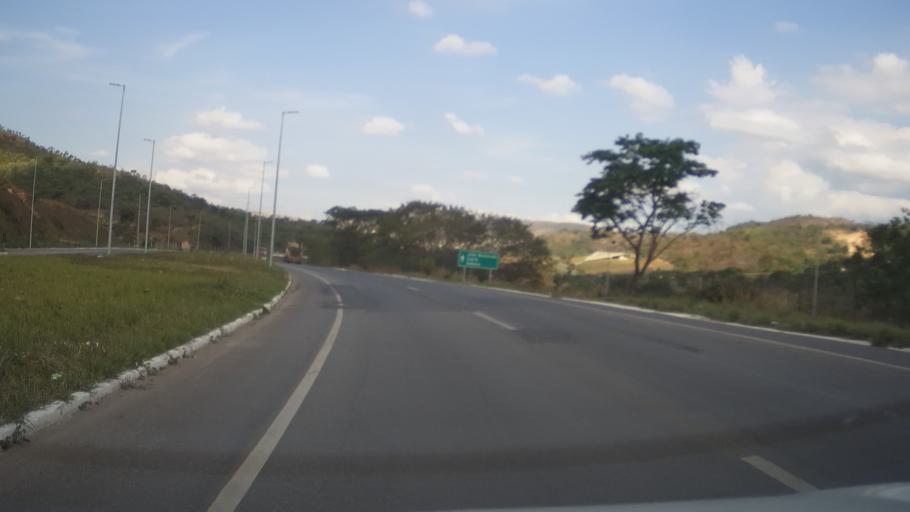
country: BR
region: Minas Gerais
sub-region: Belo Horizonte
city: Belo Horizonte
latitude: -19.8715
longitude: -43.8867
